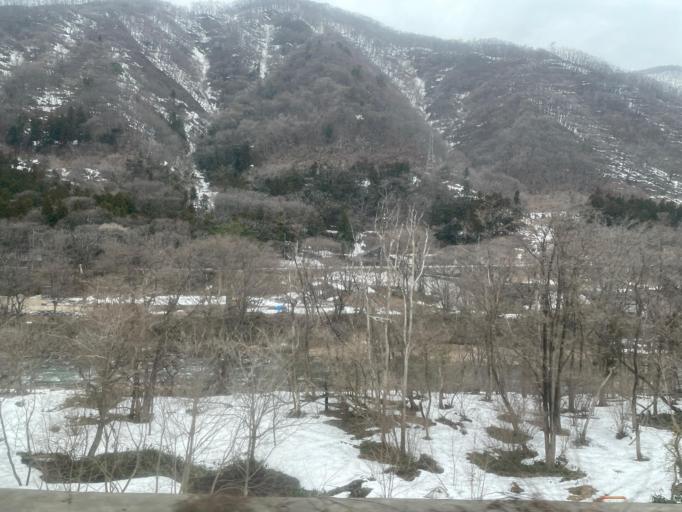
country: JP
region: Gunma
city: Numata
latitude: 36.7873
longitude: 138.9802
